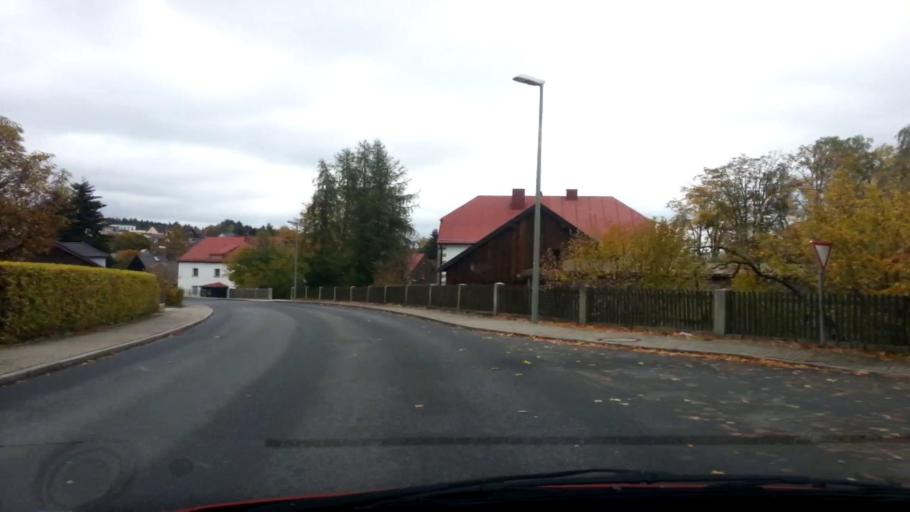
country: DE
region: Bavaria
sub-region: Upper Franconia
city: Fichtelberg
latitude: 49.9992
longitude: 11.8472
